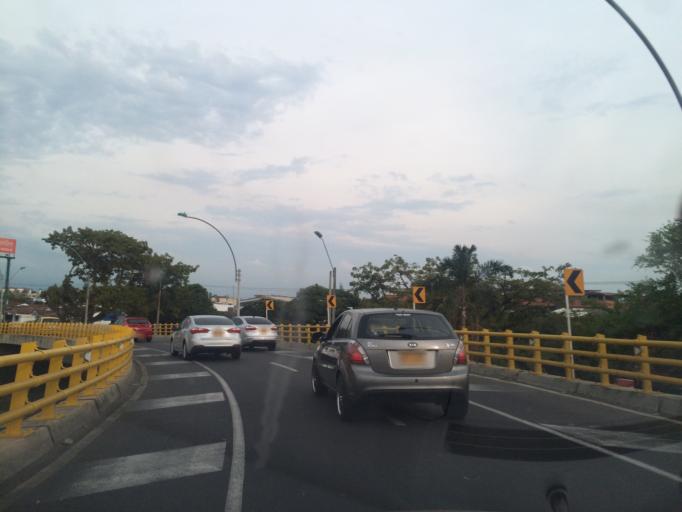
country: CO
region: Valle del Cauca
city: Cali
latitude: 3.3942
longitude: -76.5438
